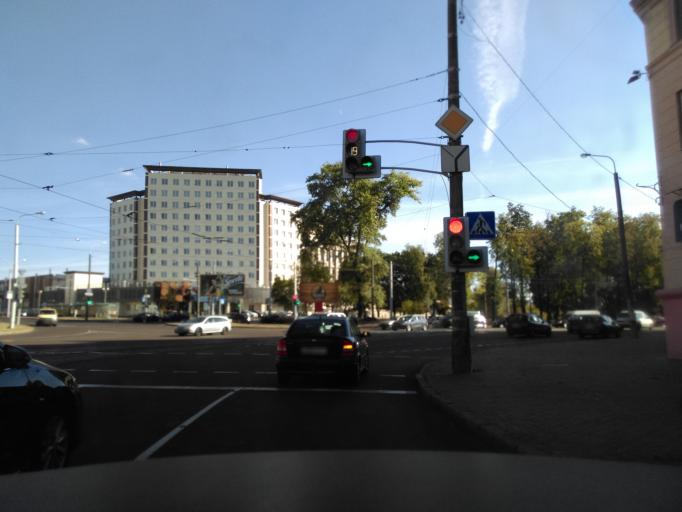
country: BY
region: Minsk
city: Minsk
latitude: 53.9051
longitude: 27.5844
